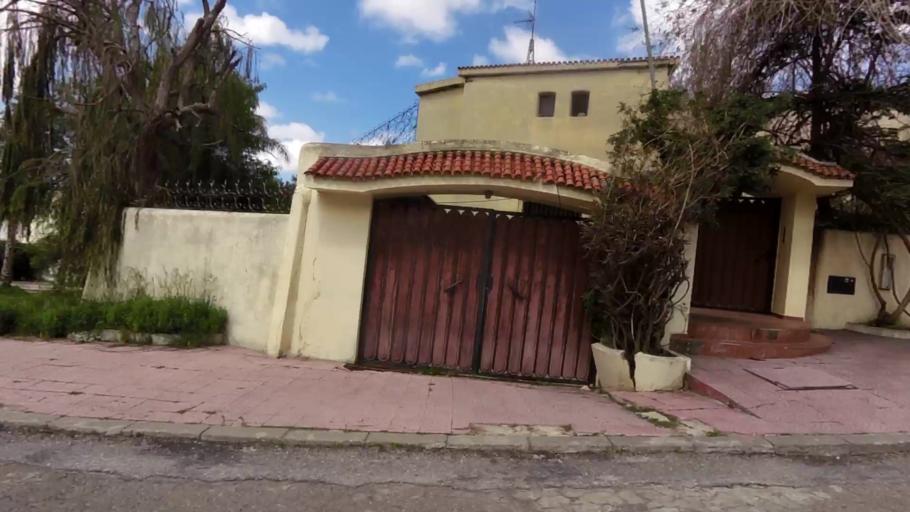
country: MA
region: Tanger-Tetouan
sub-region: Tanger-Assilah
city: Tangier
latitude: 35.7753
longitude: -5.7733
